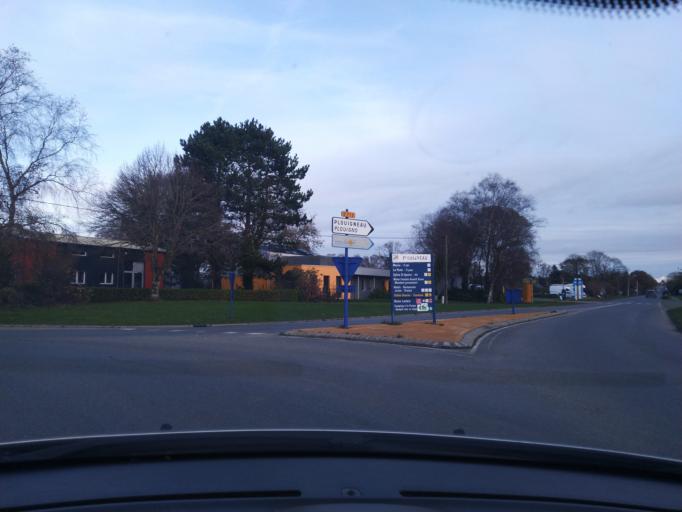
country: FR
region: Brittany
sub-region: Departement du Finistere
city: Plouigneau
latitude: 48.5711
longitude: -3.7204
